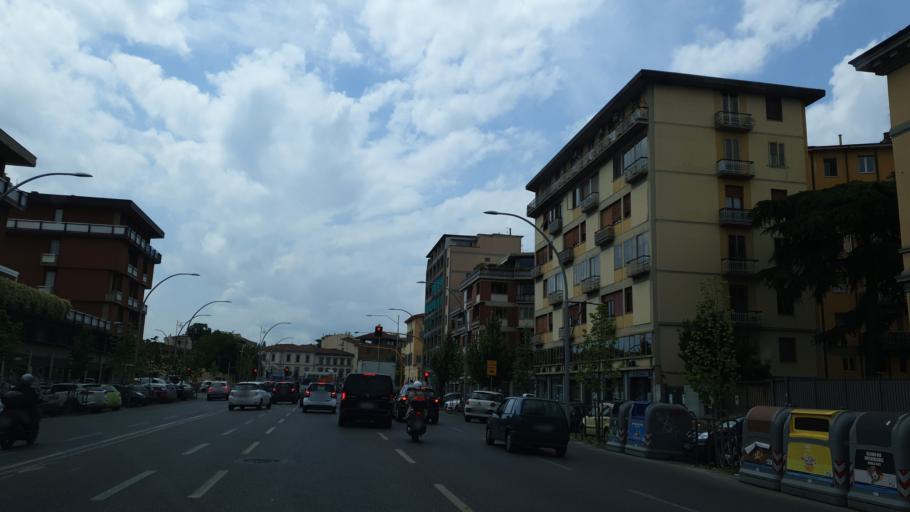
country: IT
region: Tuscany
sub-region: Province of Florence
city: Florence
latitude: 43.7797
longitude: 11.2413
